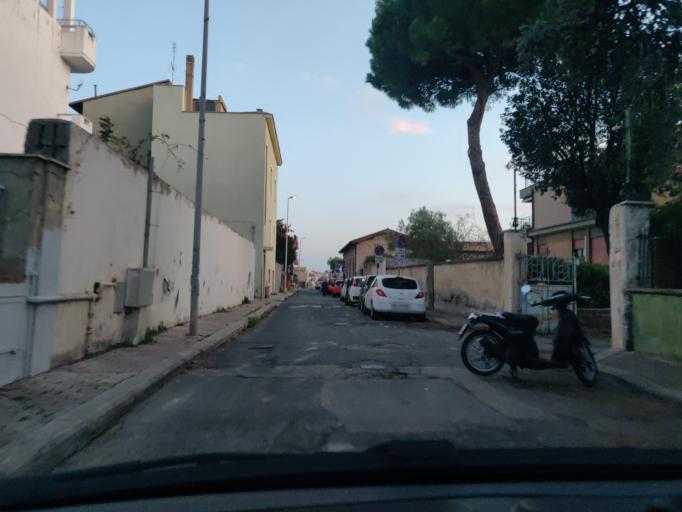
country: IT
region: Latium
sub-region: Citta metropolitana di Roma Capitale
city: Civitavecchia
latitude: 42.0830
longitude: 11.8039
